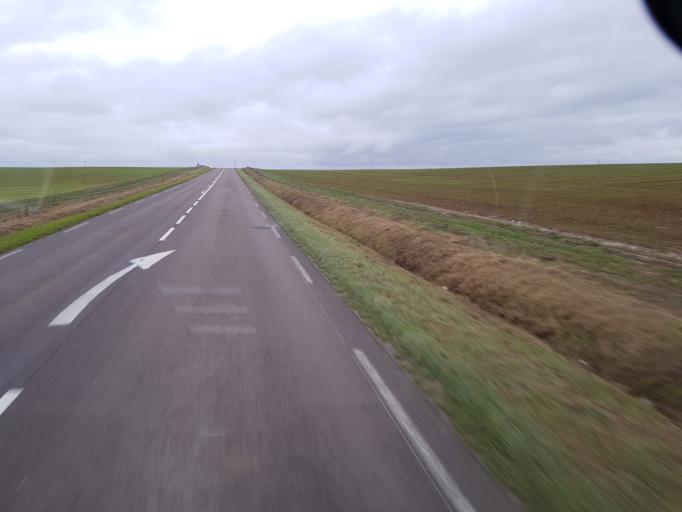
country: FR
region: Champagne-Ardenne
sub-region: Departement de la Marne
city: Sezanne
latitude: 48.7353
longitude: 3.6790
